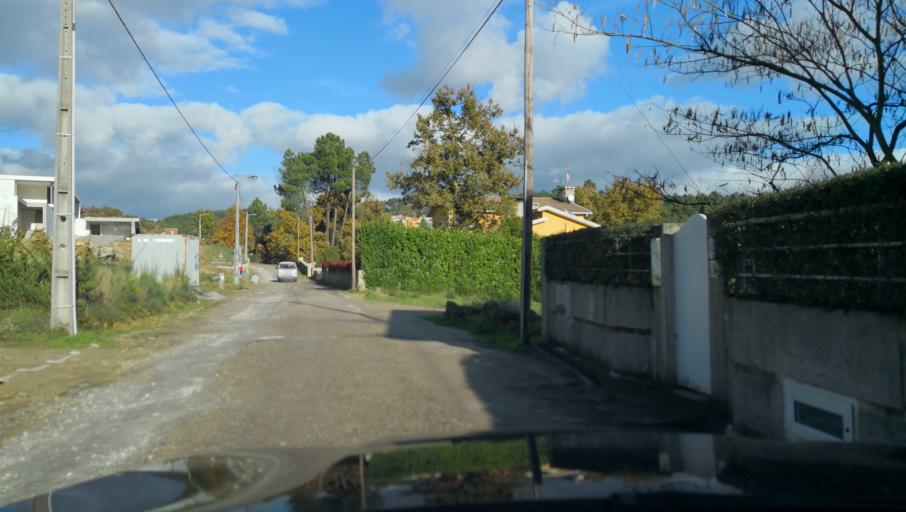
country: PT
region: Vila Real
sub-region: Vila Real
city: Vila Real
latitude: 41.3167
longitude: -7.7154
